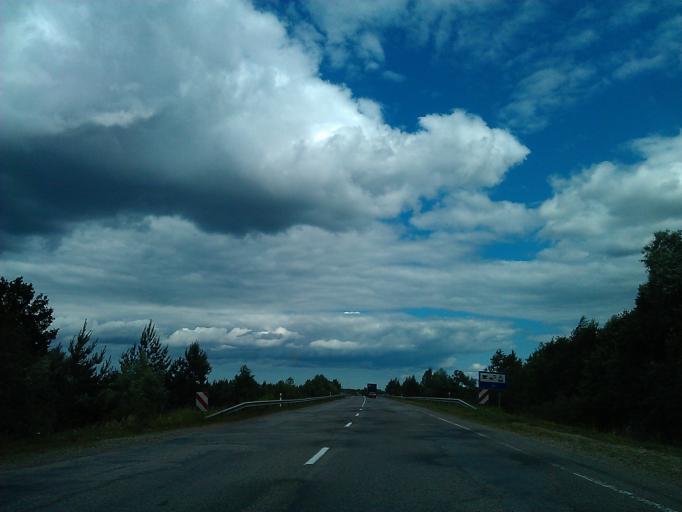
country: LV
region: Ozolnieku
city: Ozolnieki
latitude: 56.6369
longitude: 23.7720
